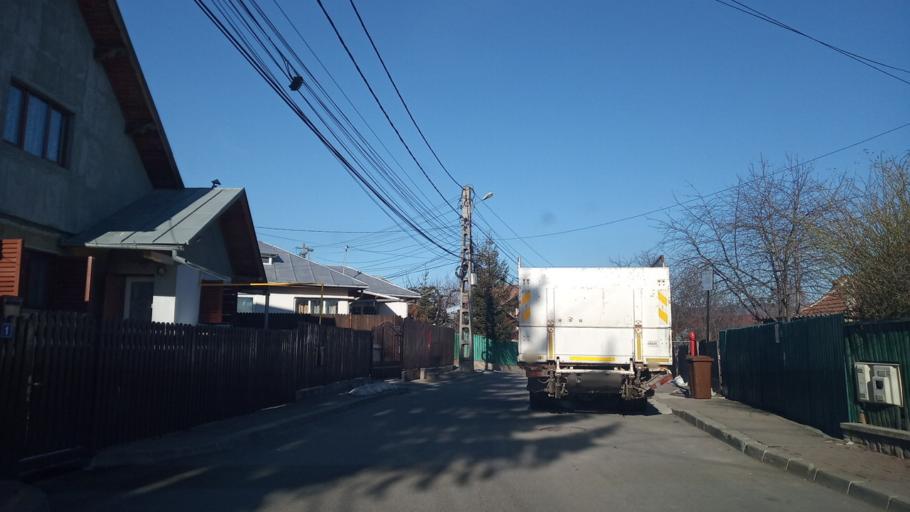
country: RO
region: Prahova
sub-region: Oras Breaza
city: Breaza
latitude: 45.1846
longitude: 25.6662
